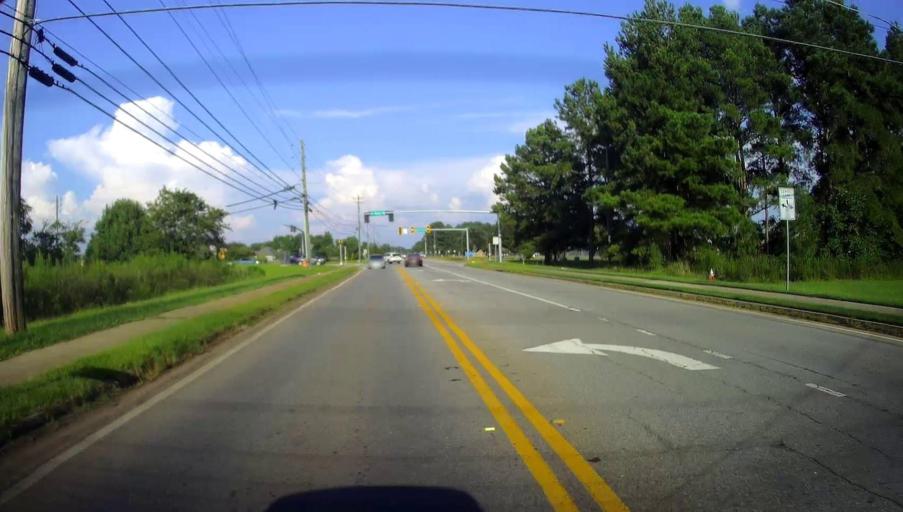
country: US
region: Georgia
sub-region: Houston County
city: Perry
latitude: 32.5062
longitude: -83.6535
